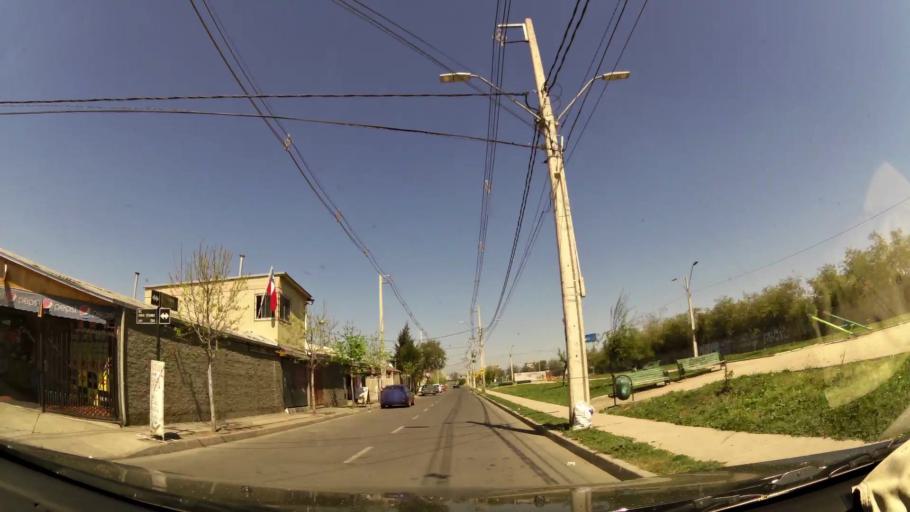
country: CL
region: Santiago Metropolitan
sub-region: Provincia de Santiago
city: Lo Prado
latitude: -33.3975
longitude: -70.7565
